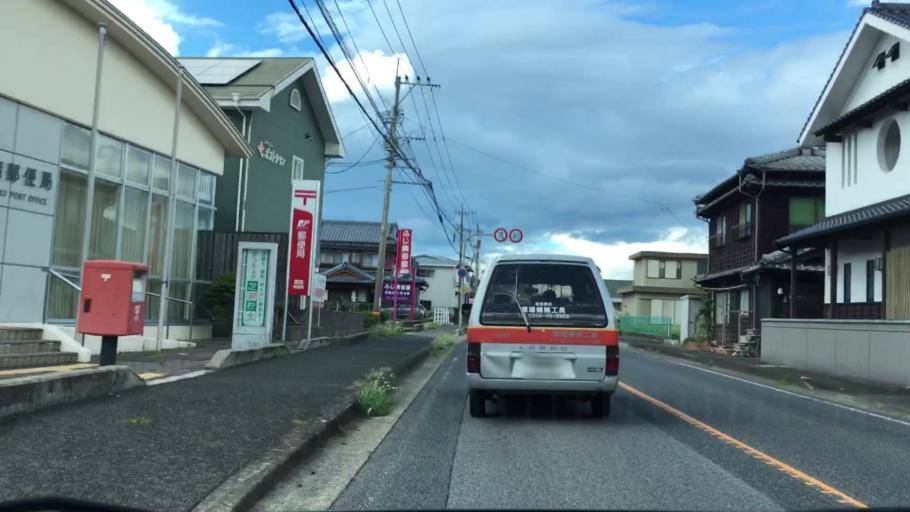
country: JP
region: Saga Prefecture
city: Imaricho-ko
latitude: 33.2022
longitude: 129.8502
